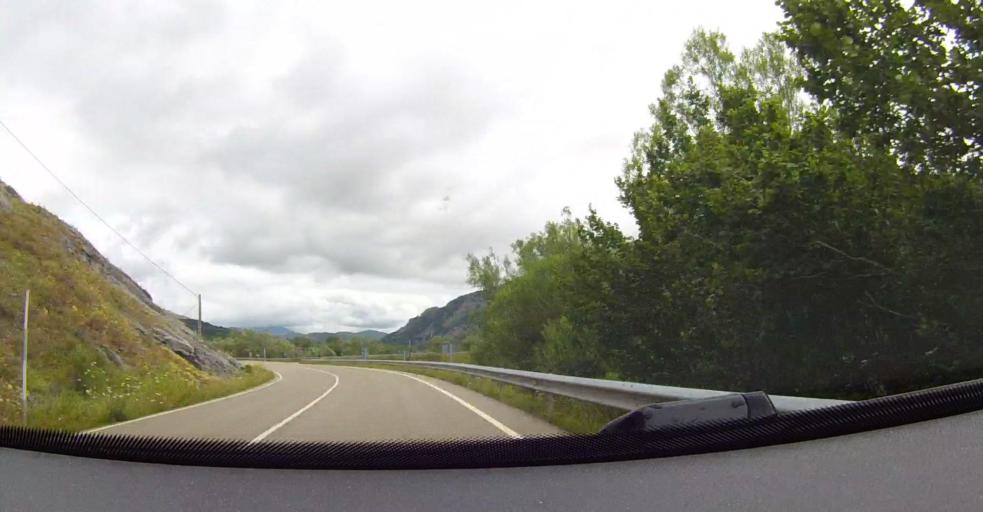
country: ES
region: Castille and Leon
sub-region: Provincia de Leon
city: Buron
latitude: 43.0268
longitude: -5.0632
